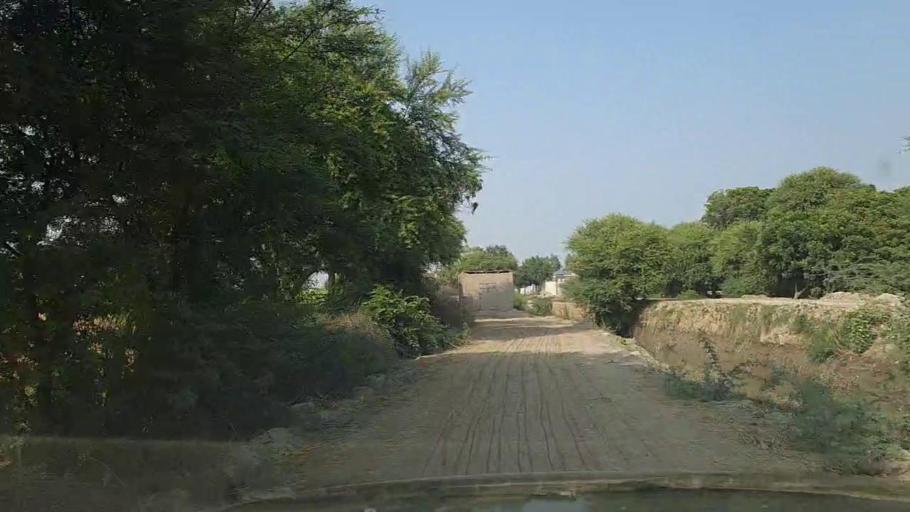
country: PK
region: Sindh
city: Mirpur Batoro
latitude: 24.6988
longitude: 68.2568
